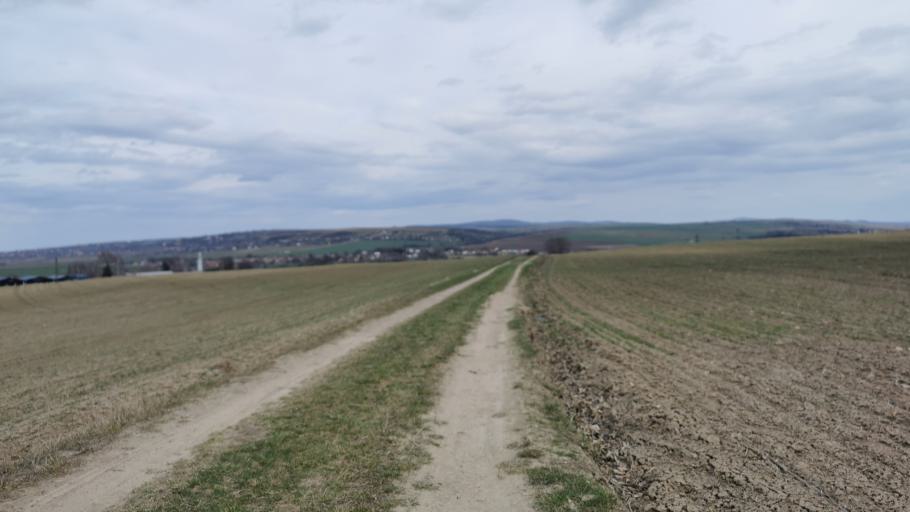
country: SK
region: Trnavsky
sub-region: Okres Skalica
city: Holic
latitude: 48.8008
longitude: 17.1737
